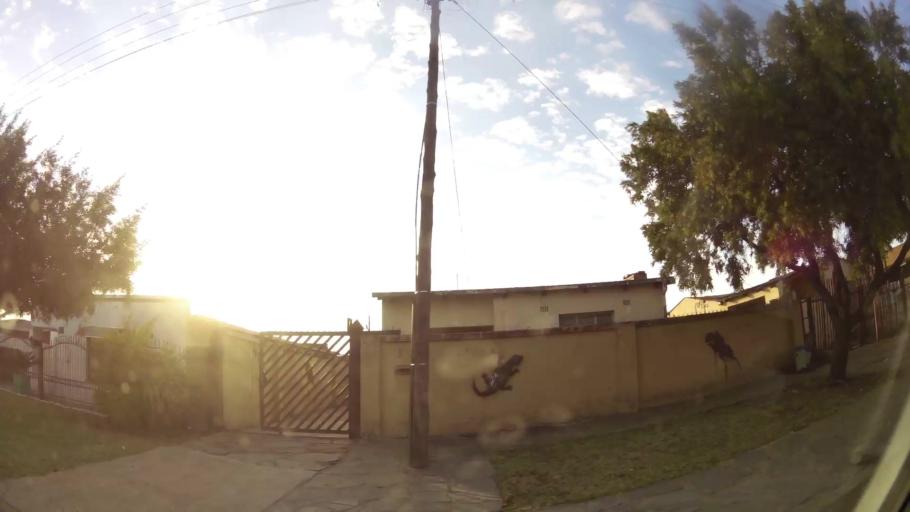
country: ZA
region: Gauteng
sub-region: City of Tshwane Metropolitan Municipality
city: Cullinan
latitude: -25.7128
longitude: 28.3701
